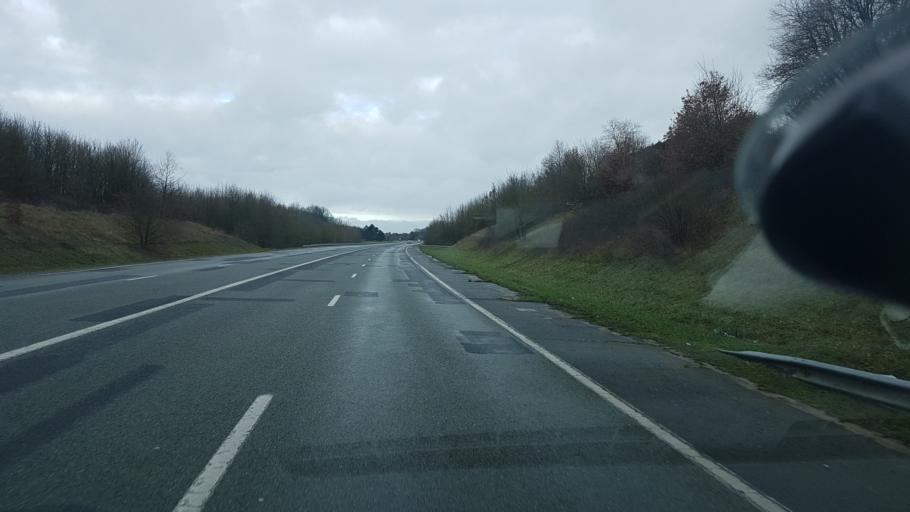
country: FR
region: Centre
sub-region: Departement du Loiret
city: Dordives
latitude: 48.1616
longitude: 2.7643
